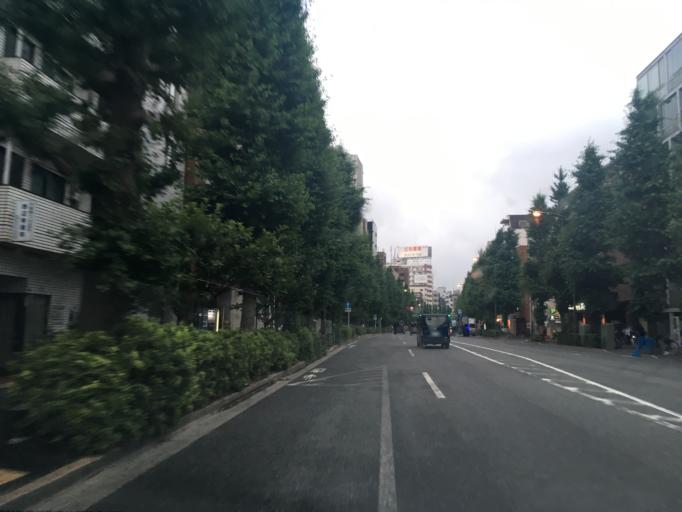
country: JP
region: Tokyo
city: Tokyo
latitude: 35.6977
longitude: 139.6434
